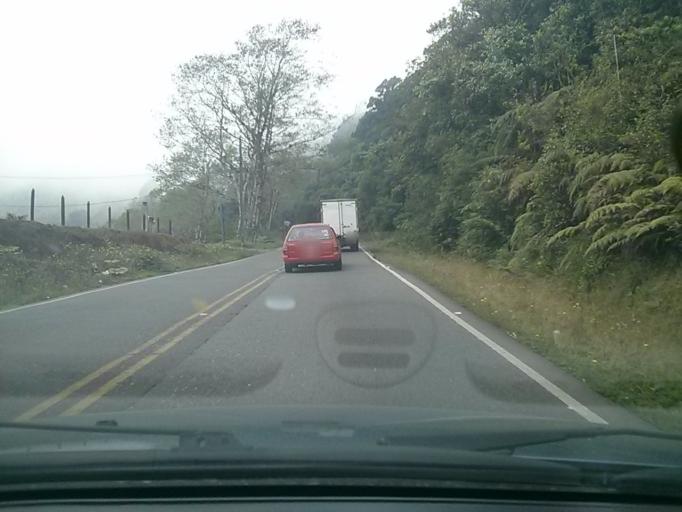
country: CR
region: Cartago
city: Tobosi
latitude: 9.7409
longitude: -83.9587
